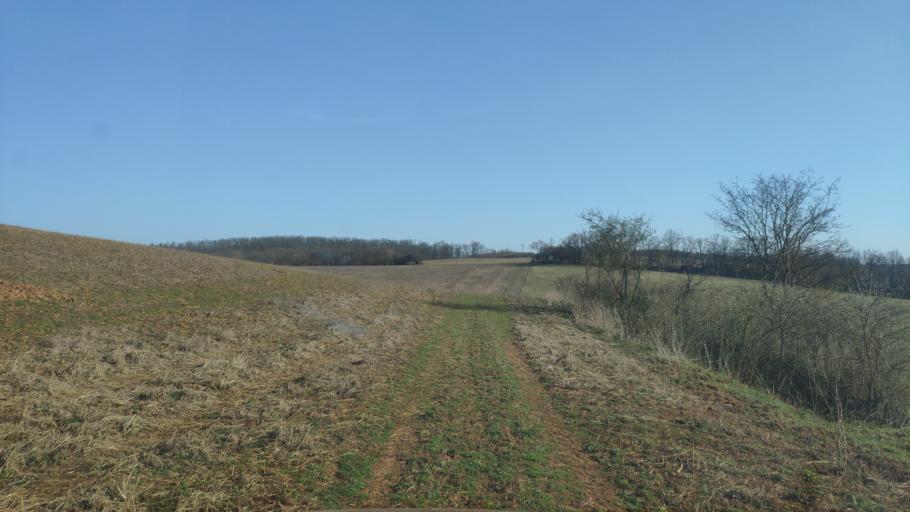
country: SK
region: Banskobystricky
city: Revuca
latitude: 48.5462
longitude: 20.2550
